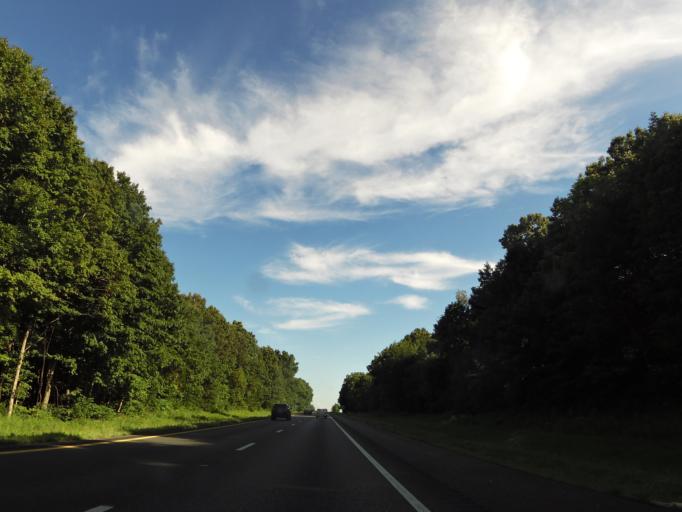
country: US
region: Tennessee
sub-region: Montgomery County
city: Clarksville
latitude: 36.5644
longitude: -87.2544
